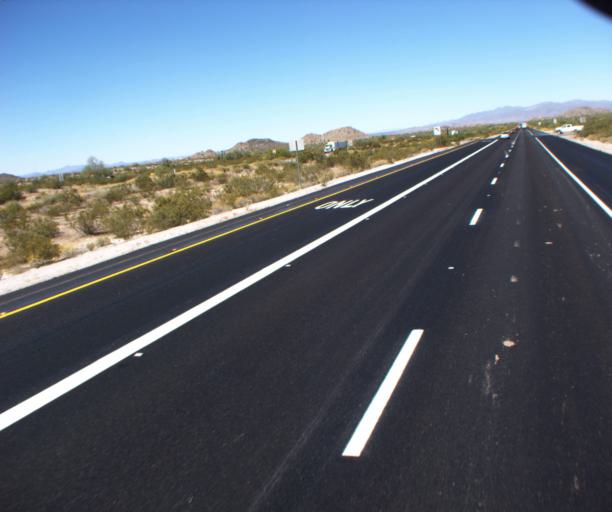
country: US
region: Arizona
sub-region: Maricopa County
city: Buckeye
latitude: 33.2746
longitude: -112.6320
